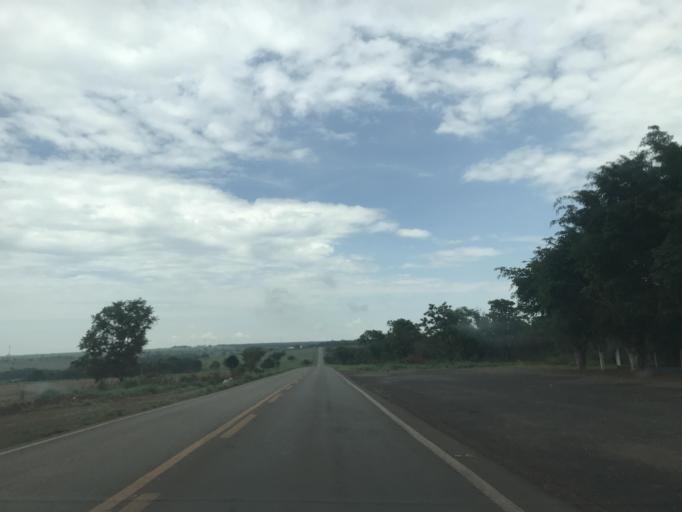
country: BR
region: Goias
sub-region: Luziania
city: Luziania
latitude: -16.2671
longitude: -47.9813
